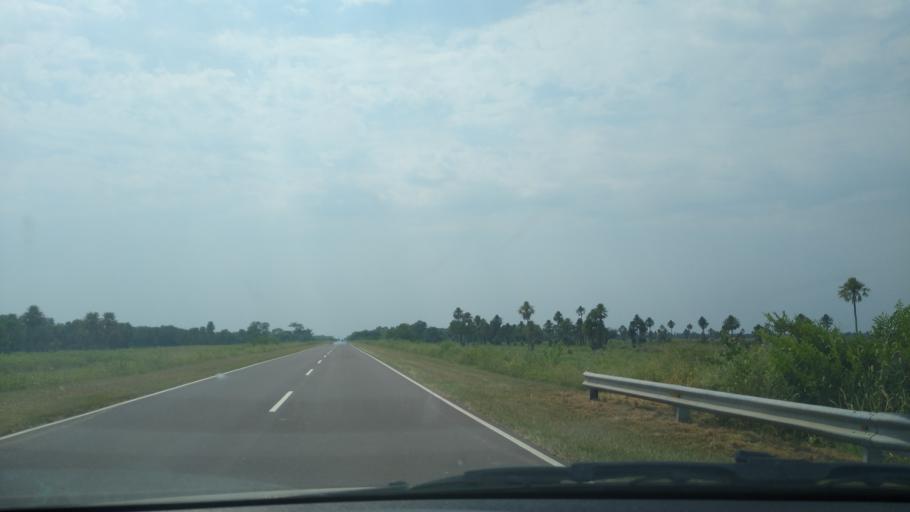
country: AR
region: Chaco
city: La Eduvigis
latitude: -27.0323
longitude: -58.9656
